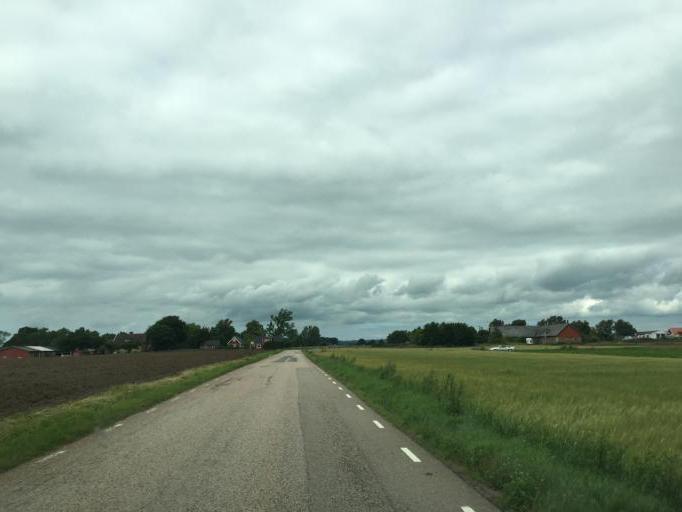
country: SE
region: Skane
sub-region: Angelholms Kommun
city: Vejbystrand
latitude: 56.3214
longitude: 12.7757
